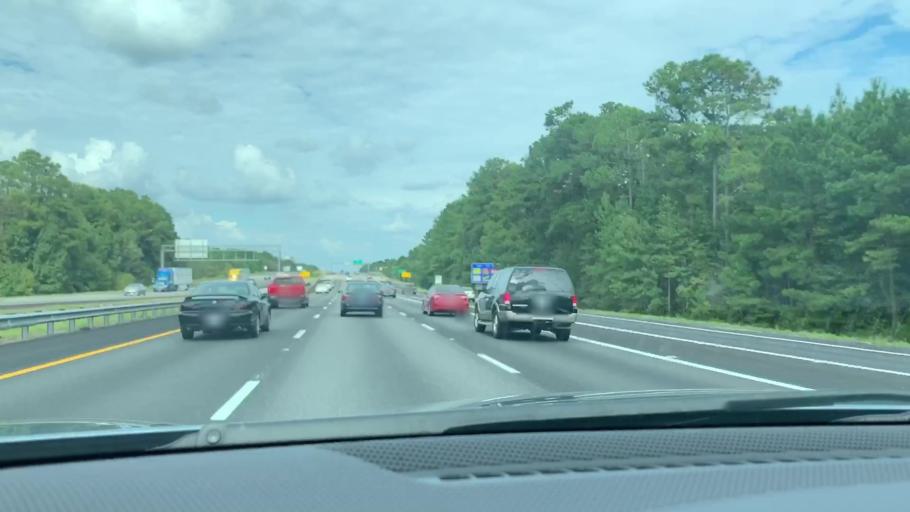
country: US
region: Georgia
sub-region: Chatham County
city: Port Wentworth
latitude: 32.1710
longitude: -81.2114
